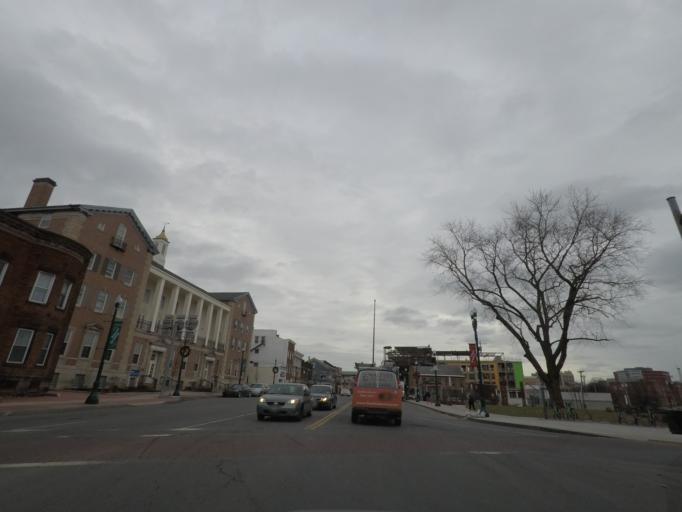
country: US
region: New York
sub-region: Schenectady County
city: Schenectady
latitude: 42.8153
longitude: -73.9491
